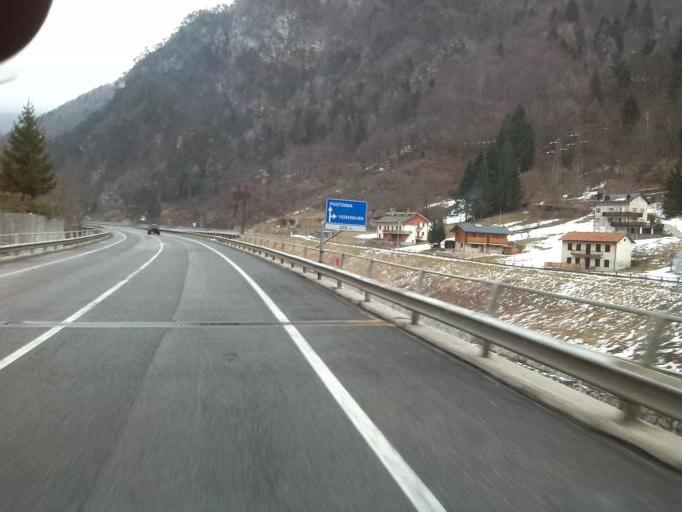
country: IT
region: Friuli Venezia Giulia
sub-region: Provincia di Udine
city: Pontebba
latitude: 46.4801
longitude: 13.2983
